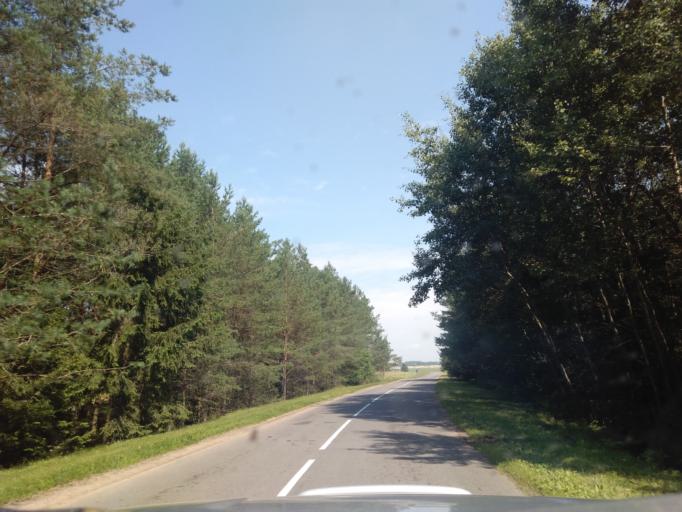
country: BY
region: Minsk
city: Valozhyn
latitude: 54.0286
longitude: 26.6034
